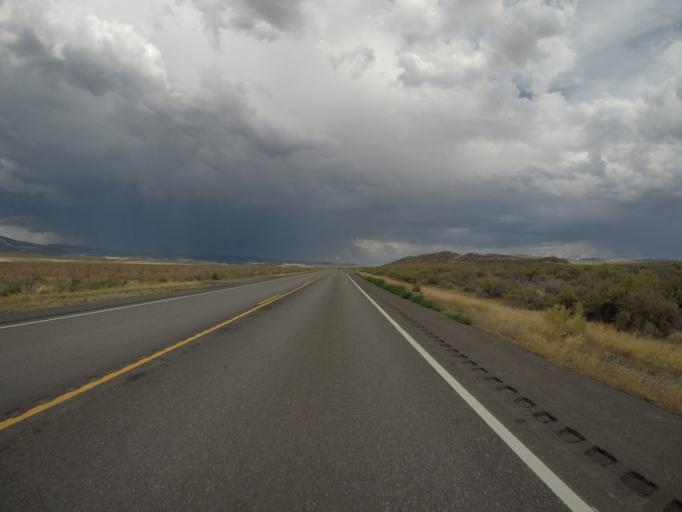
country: US
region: Utah
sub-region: Uintah County
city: Naples
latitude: 40.2906
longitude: -109.1630
